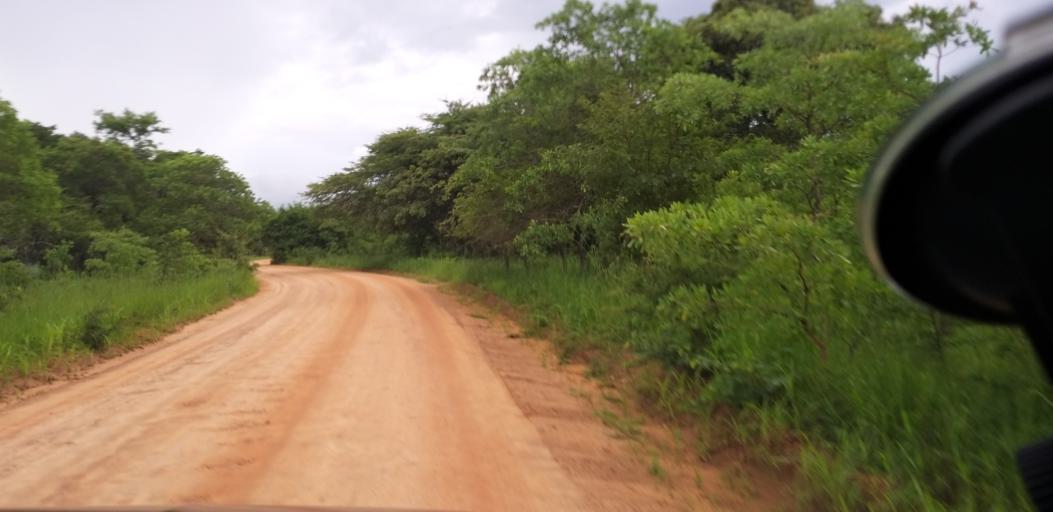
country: ZM
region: Lusaka
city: Chongwe
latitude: -15.1552
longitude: 28.4979
